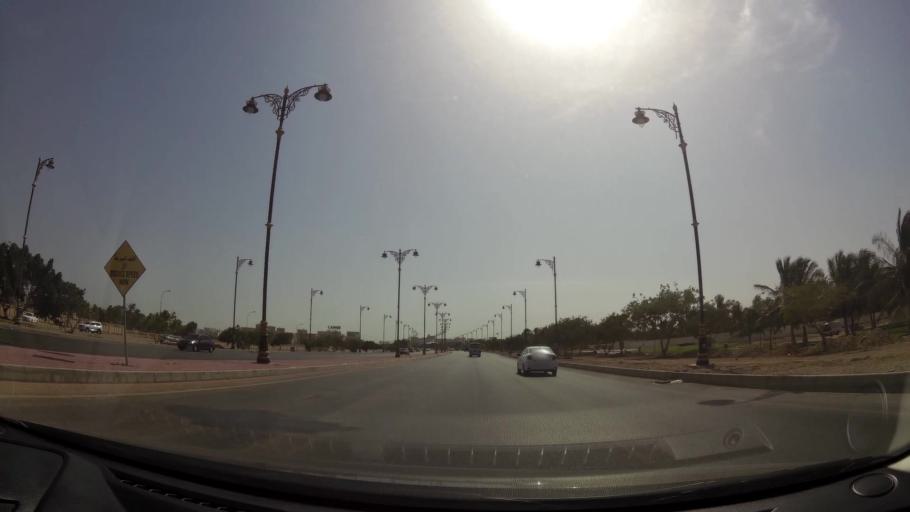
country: OM
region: Zufar
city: Salalah
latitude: 17.0232
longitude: 54.0745
